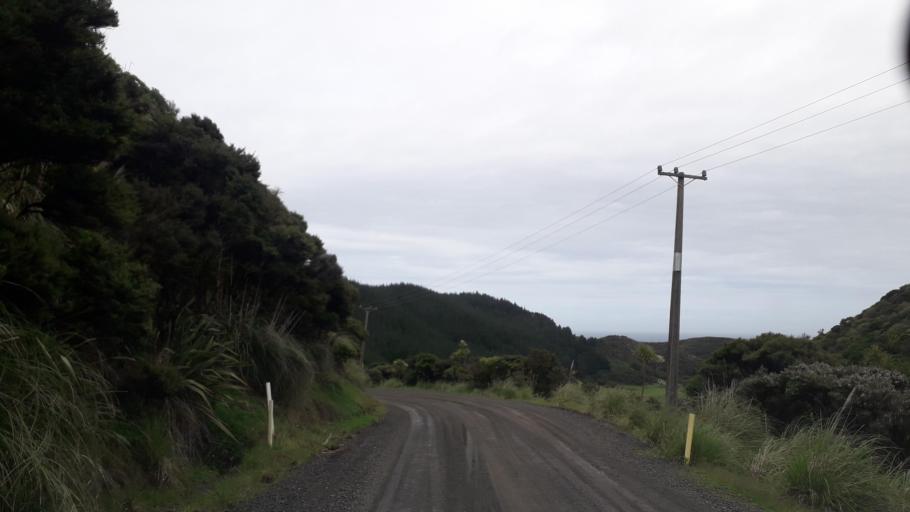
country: NZ
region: Northland
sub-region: Far North District
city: Ahipara
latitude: -35.4387
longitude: 173.3044
